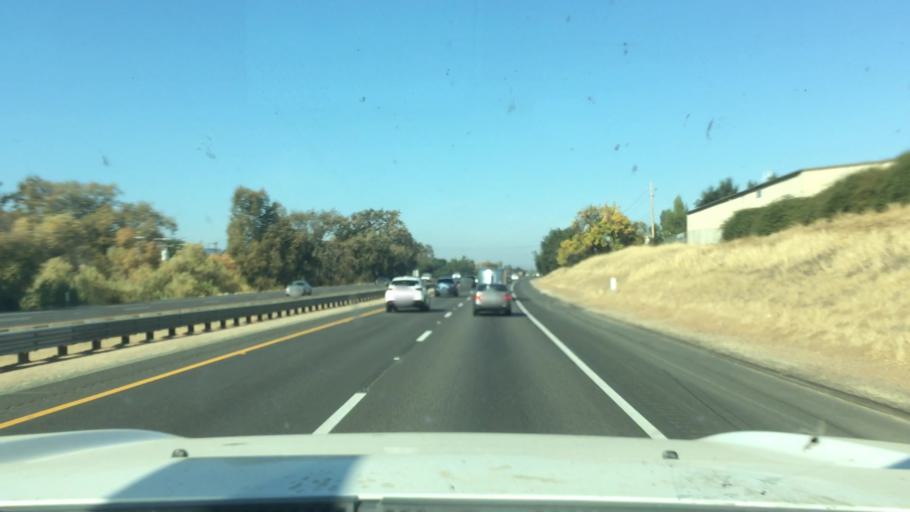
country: US
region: California
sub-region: San Luis Obispo County
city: Atascadero
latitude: 35.5032
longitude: -120.6911
